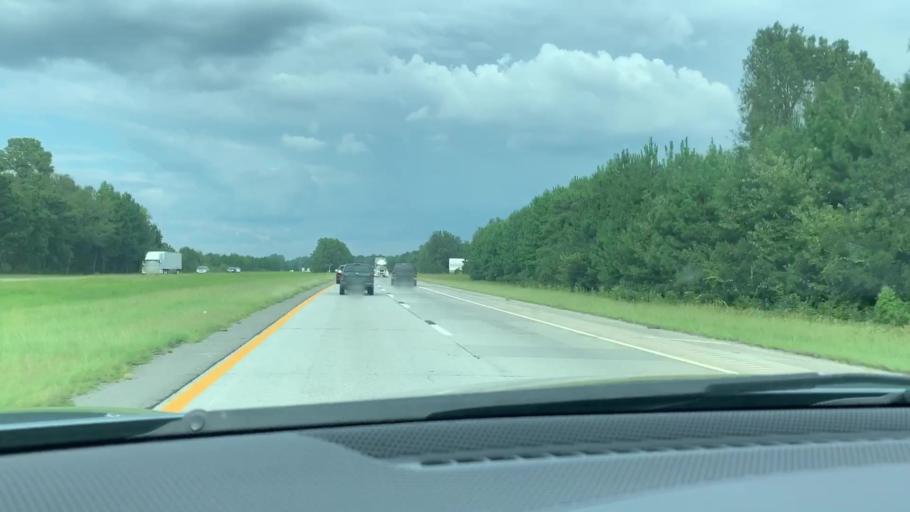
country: US
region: South Carolina
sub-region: Dorchester County
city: Saint George
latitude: 33.1348
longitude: -80.6343
